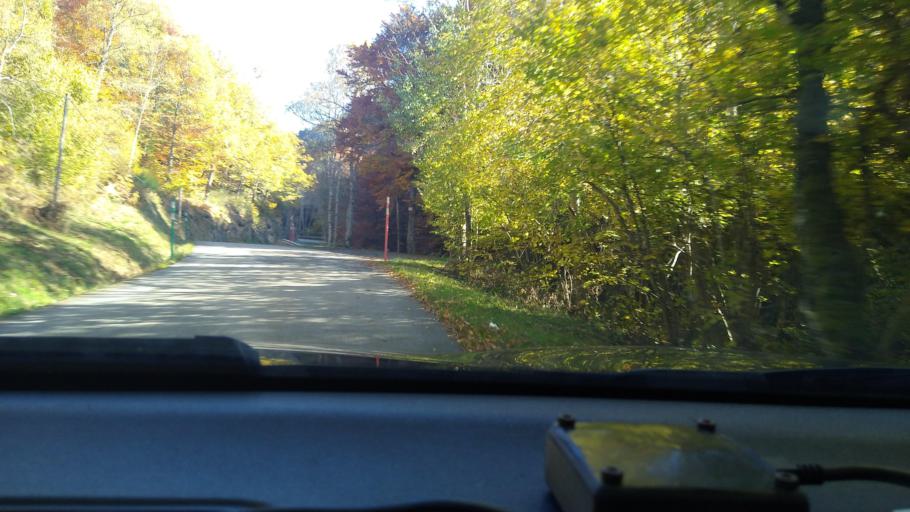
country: FR
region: Midi-Pyrenees
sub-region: Departement de l'Ariege
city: Ax-les-Thermes
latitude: 42.7186
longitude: 1.9120
